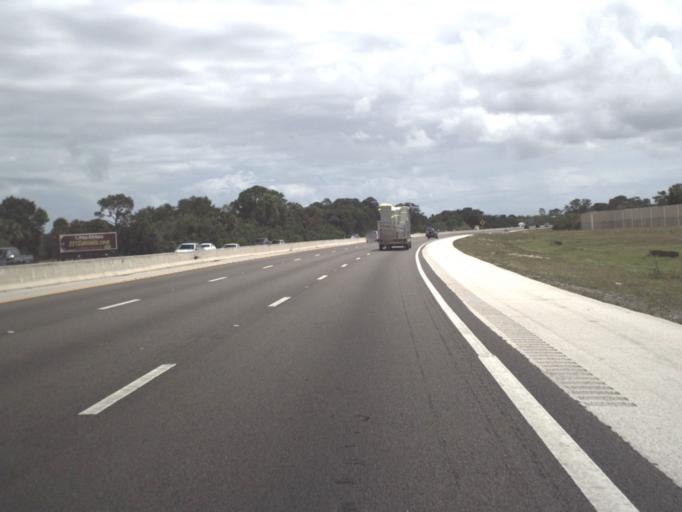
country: US
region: Florida
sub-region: Brevard County
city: Rockledge
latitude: 28.2906
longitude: -80.7403
